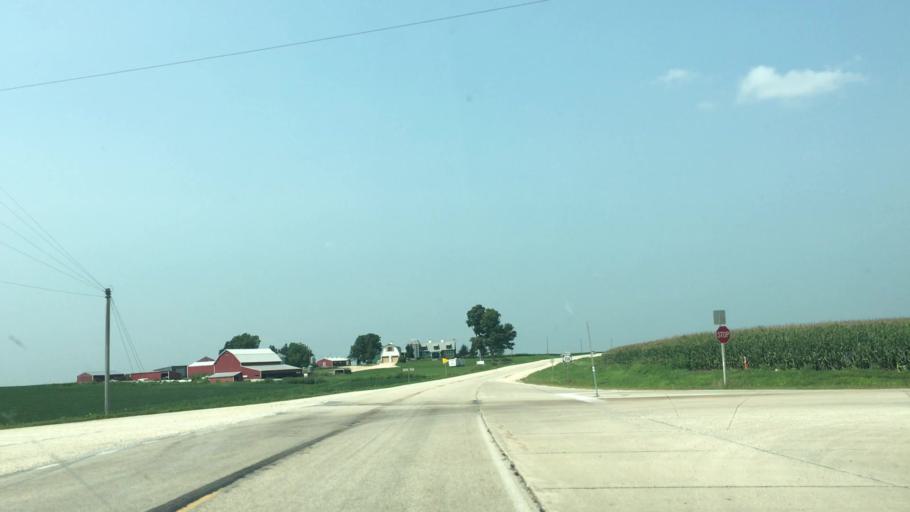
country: US
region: Iowa
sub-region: Fayette County
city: West Union
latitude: 42.9786
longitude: -91.8231
